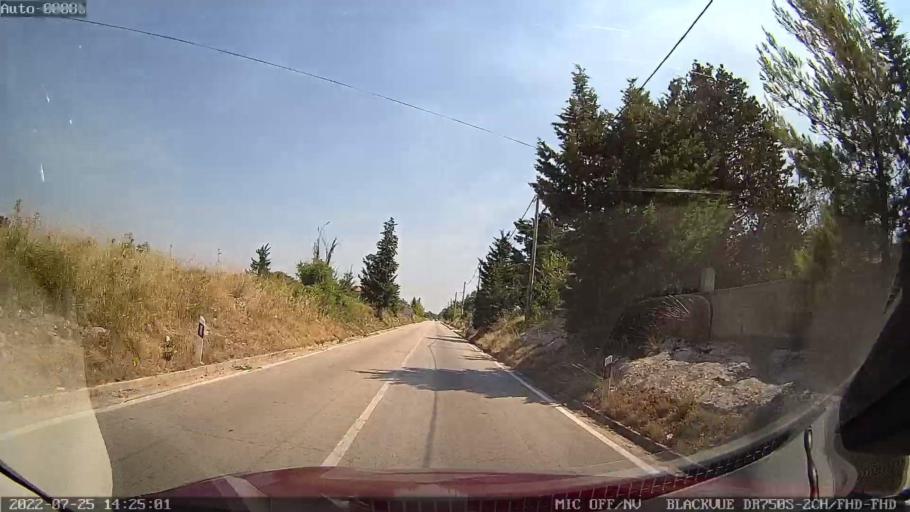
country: HR
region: Zadarska
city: Policnik
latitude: 44.1472
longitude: 15.3275
